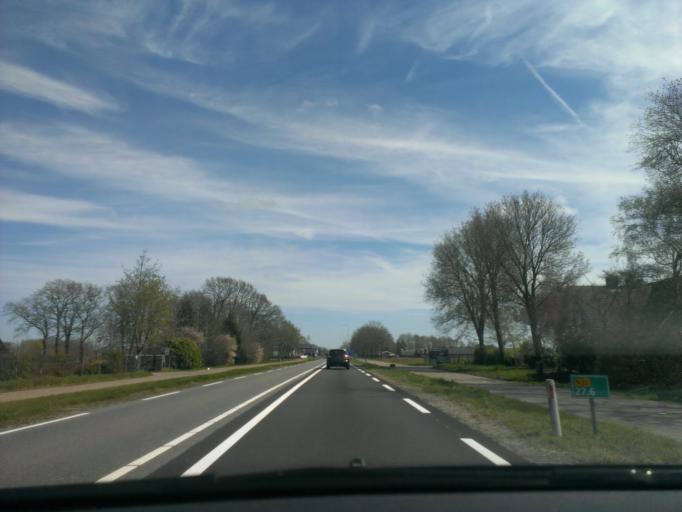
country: NL
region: Overijssel
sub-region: Gemeente Raalte
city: Raalte
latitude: 52.3711
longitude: 6.3717
